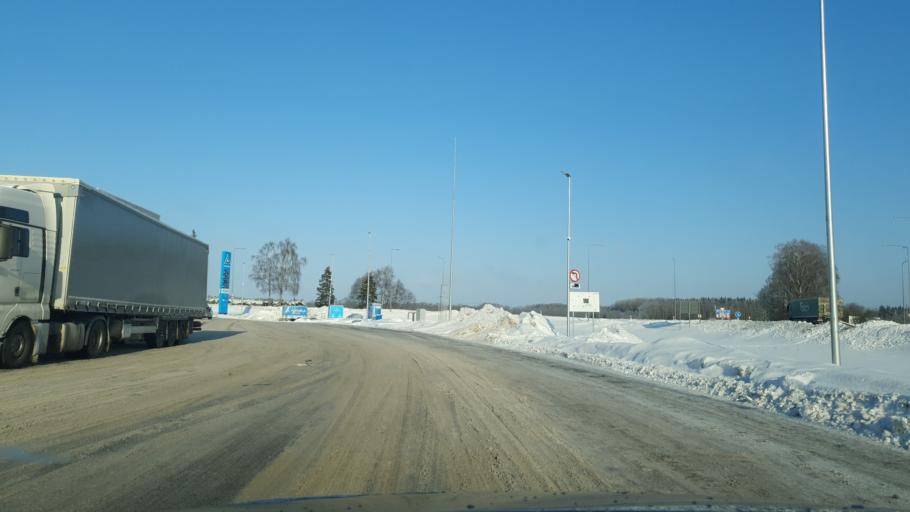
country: EE
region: Jogevamaa
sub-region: Poltsamaa linn
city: Poltsamaa
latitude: 58.7448
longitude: 25.7688
